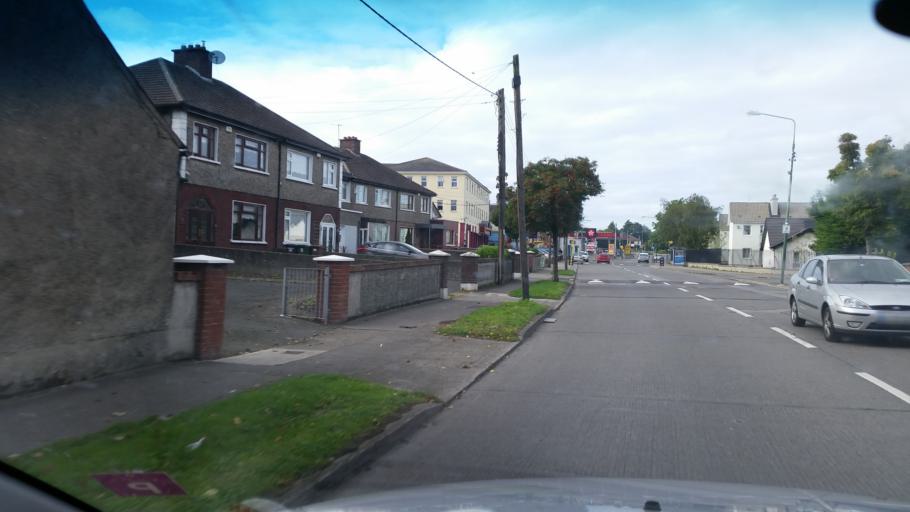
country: IE
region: Leinster
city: Glasnevin
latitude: 53.3812
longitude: -6.2762
